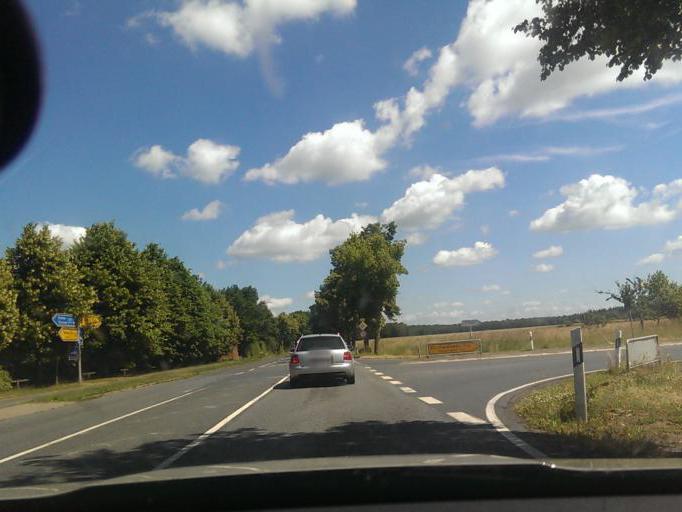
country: DE
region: Lower Saxony
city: Verden
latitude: 52.9792
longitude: 9.2588
